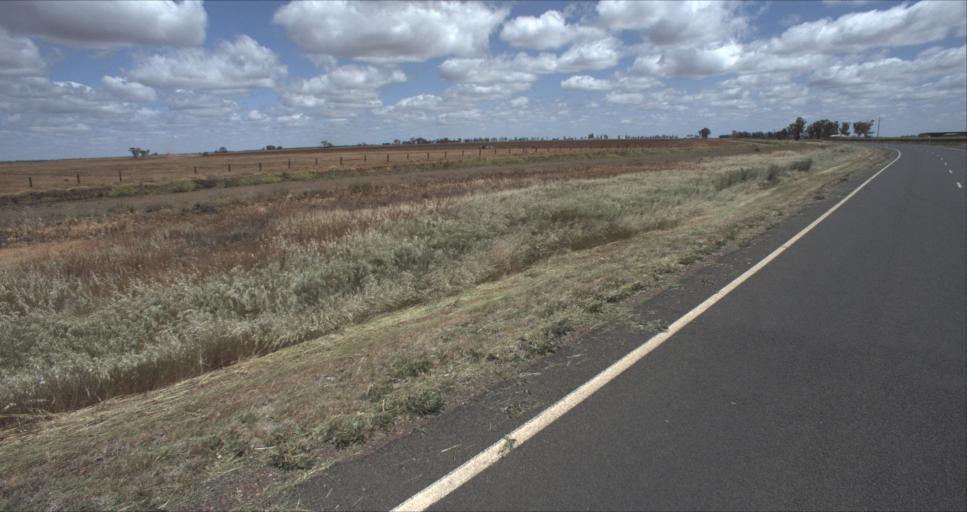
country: AU
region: New South Wales
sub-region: Murrumbidgee Shire
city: Darlington Point
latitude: -34.4764
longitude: 146.1496
